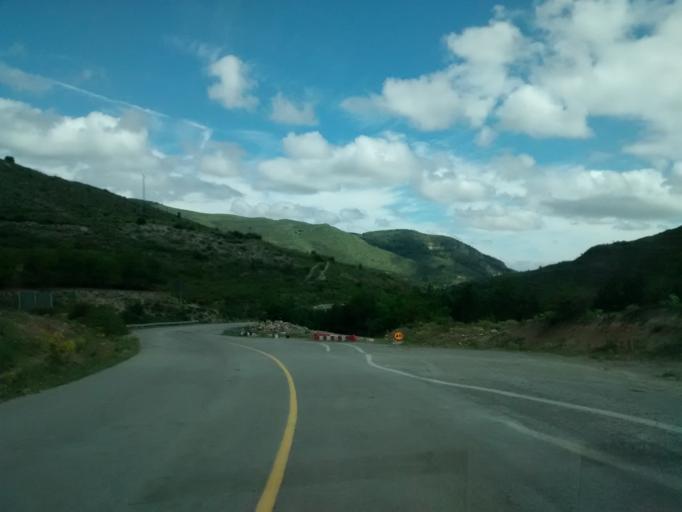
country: ES
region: La Rioja
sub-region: Provincia de La Rioja
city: Terroba
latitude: 42.2690
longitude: -2.4329
